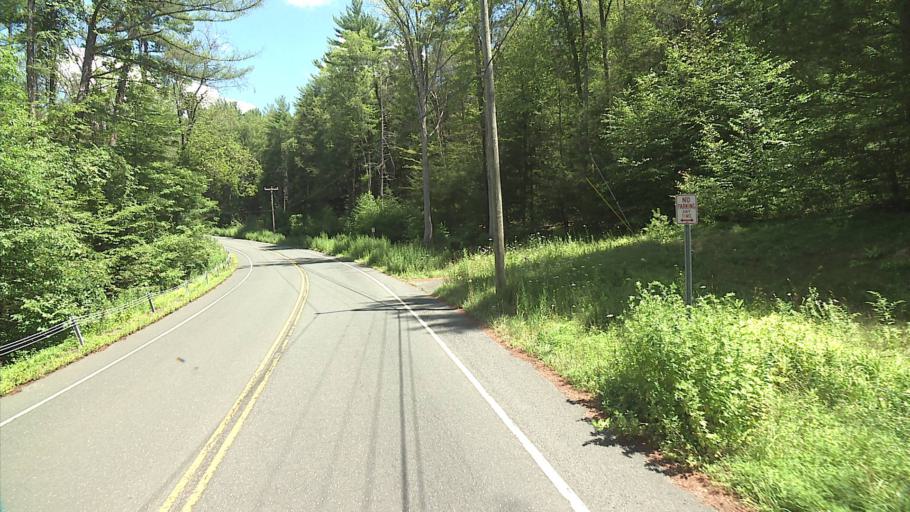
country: US
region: Connecticut
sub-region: Litchfield County
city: New Hartford Center
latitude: 41.9052
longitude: -72.9536
